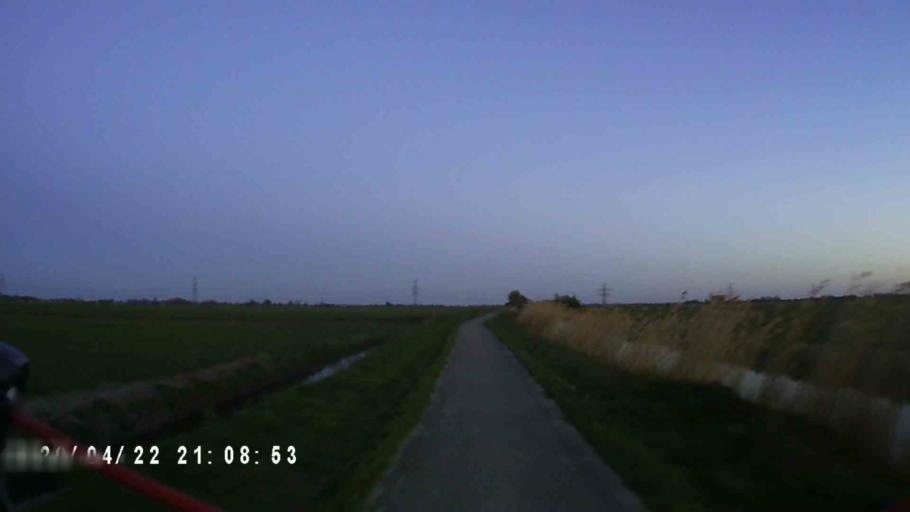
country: NL
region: Groningen
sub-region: Gemeente Winsum
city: Winsum
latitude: 53.3127
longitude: 6.5604
